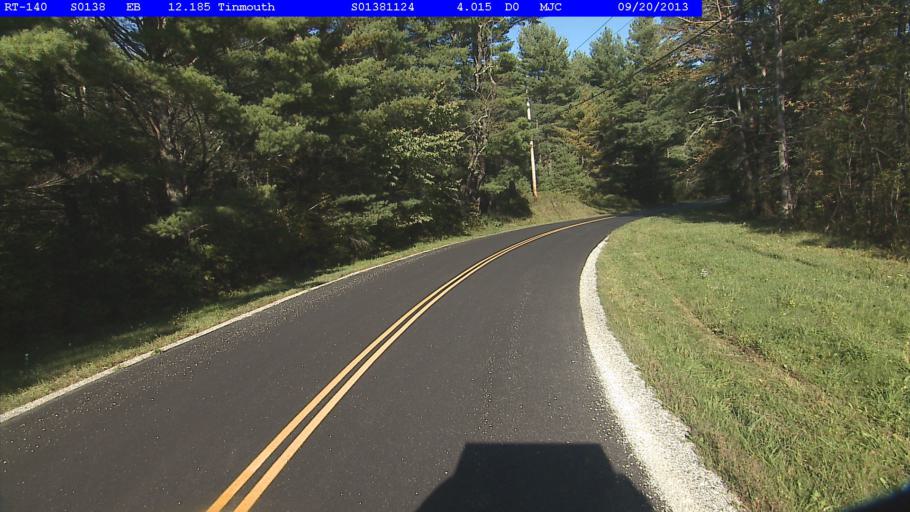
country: US
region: Vermont
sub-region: Rutland County
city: West Rutland
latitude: 43.4494
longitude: -73.0375
